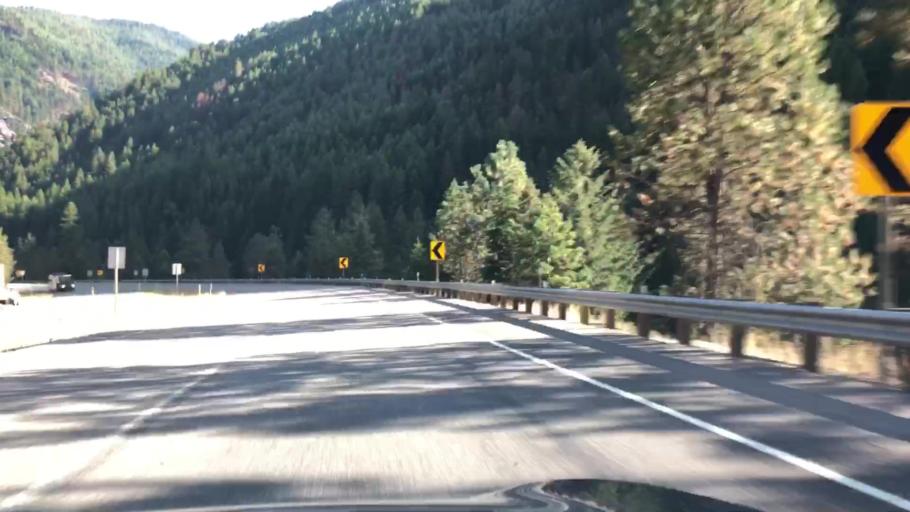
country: US
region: Montana
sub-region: Sanders County
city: Thompson Falls
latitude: 47.3180
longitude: -115.2441
